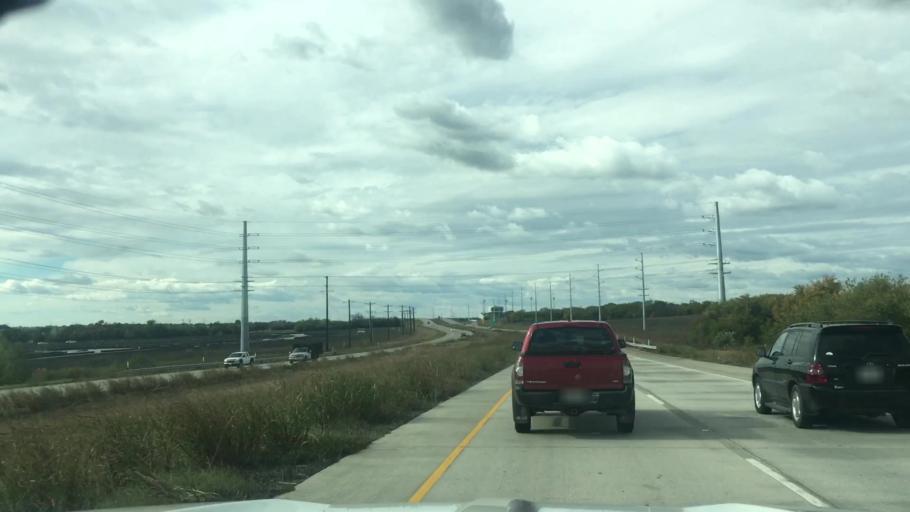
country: US
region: Texas
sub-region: Denton County
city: Denton
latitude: 33.2518
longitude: -97.0990
